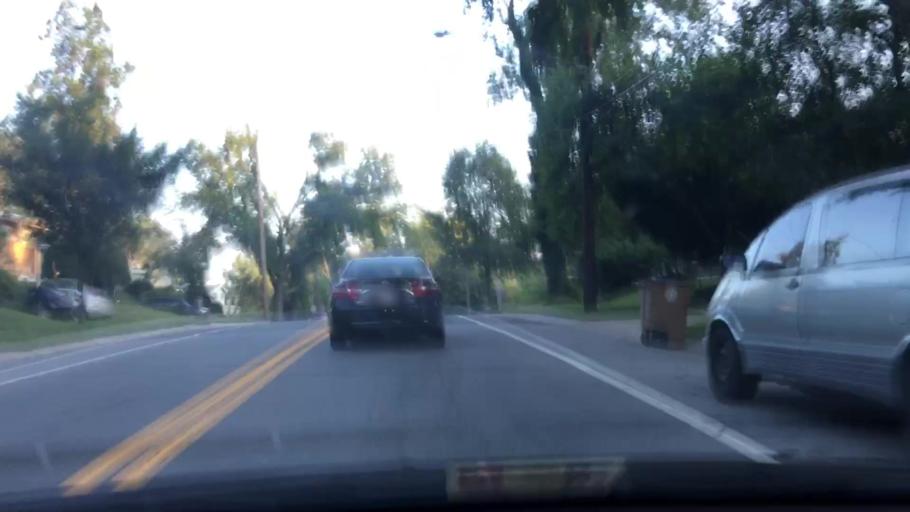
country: US
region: Maryland
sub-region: Montgomery County
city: North Bethesda
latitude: 39.0798
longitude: -77.1132
